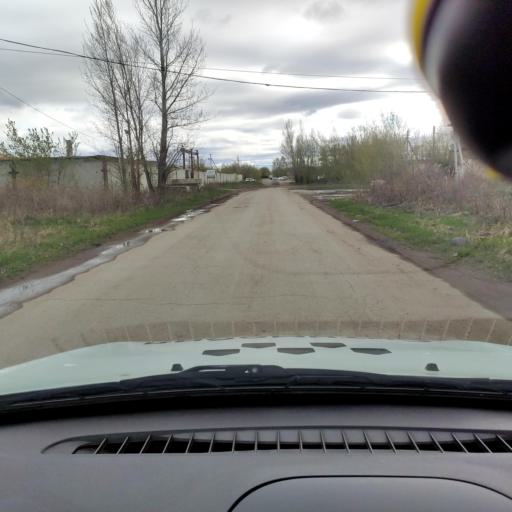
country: RU
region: Samara
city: Tol'yatti
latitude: 53.5803
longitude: 49.3140
